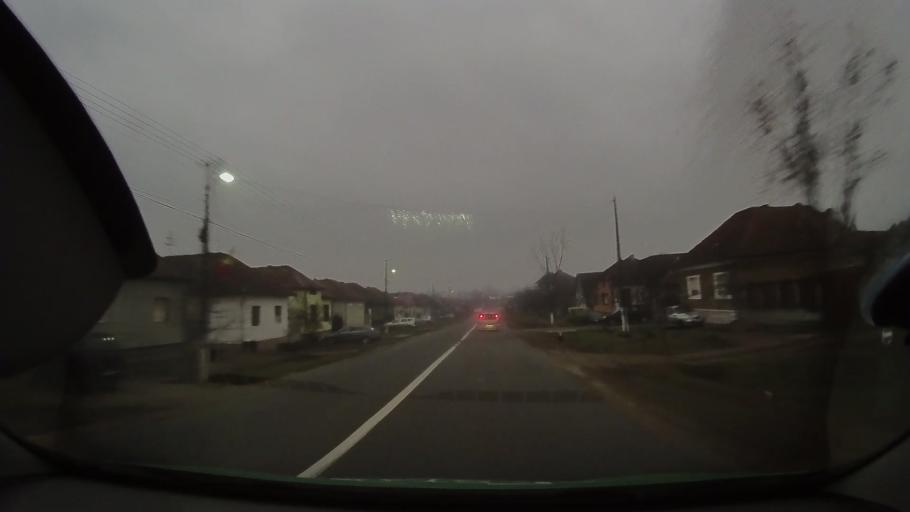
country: RO
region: Arad
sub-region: Comuna Beliu
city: Beliu
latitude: 46.4966
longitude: 21.9769
